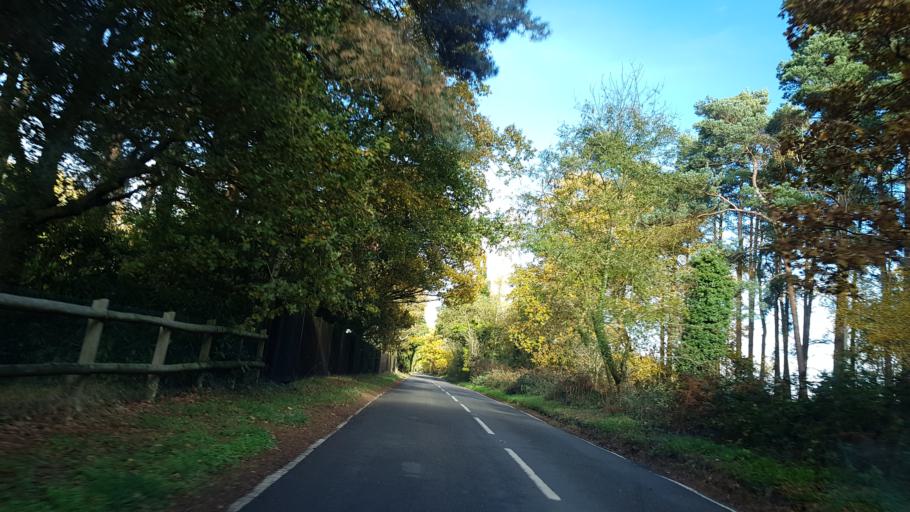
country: GB
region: England
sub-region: Surrey
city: Elstead
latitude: 51.1598
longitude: -0.7173
